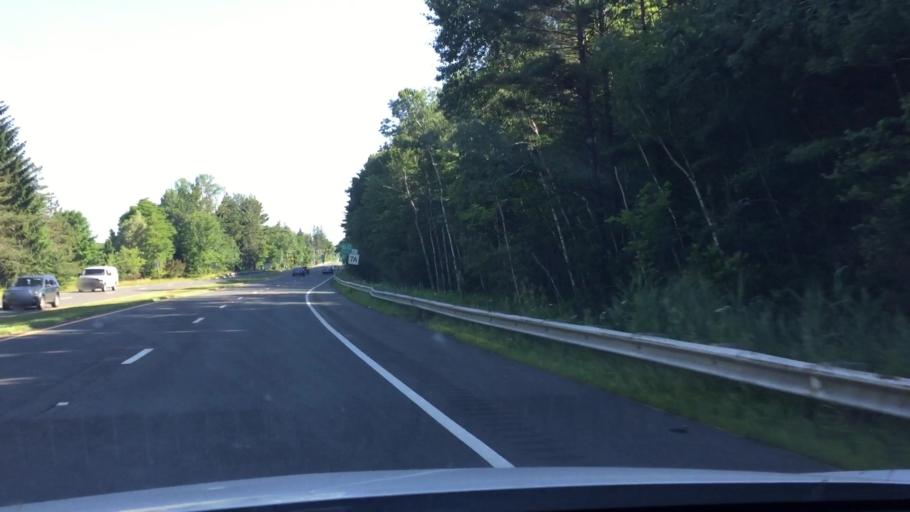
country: US
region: Massachusetts
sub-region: Berkshire County
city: Lenox
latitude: 42.3693
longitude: -73.2774
